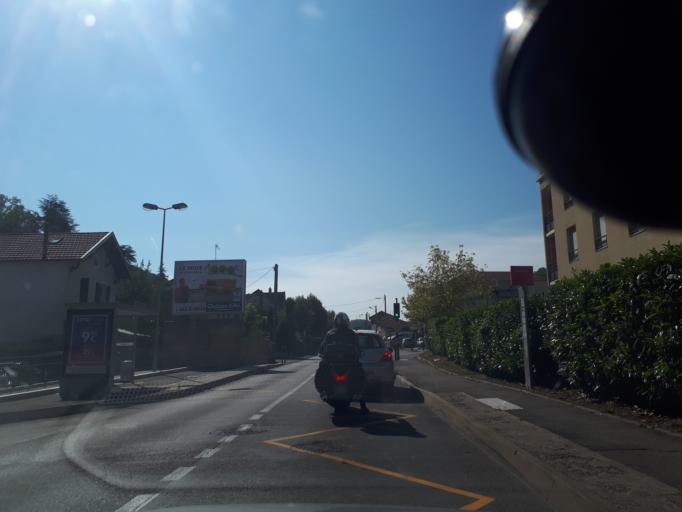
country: FR
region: Rhone-Alpes
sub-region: Departement de l'Isere
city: Bourgoin-Jallieu
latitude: 45.5801
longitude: 5.2742
